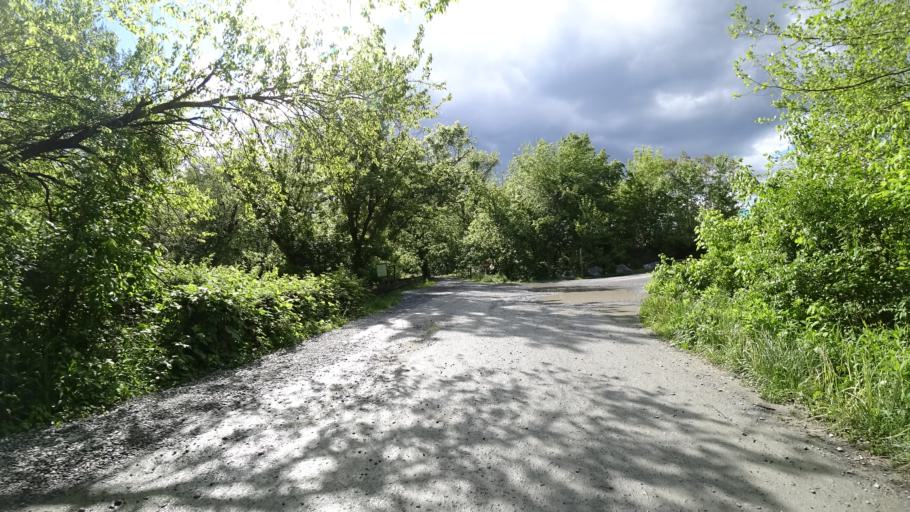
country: US
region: Maryland
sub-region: Frederick County
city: Brunswick
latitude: 39.3109
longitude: -77.6272
